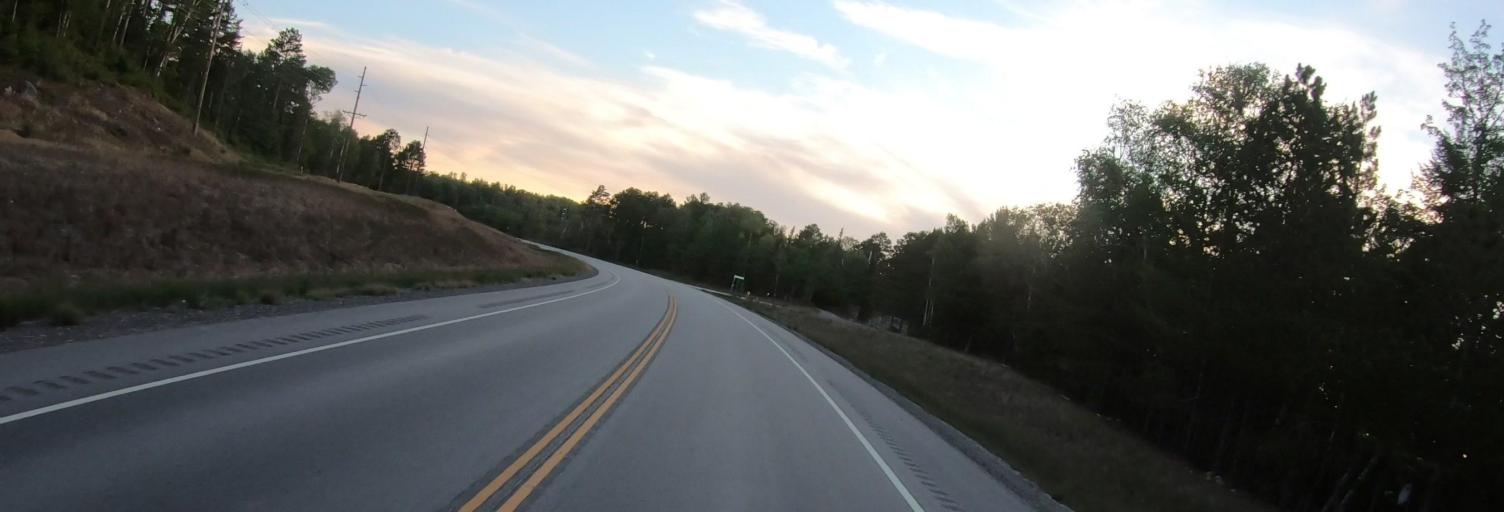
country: US
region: Minnesota
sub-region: Saint Louis County
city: Babbitt
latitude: 47.8571
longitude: -92.0764
